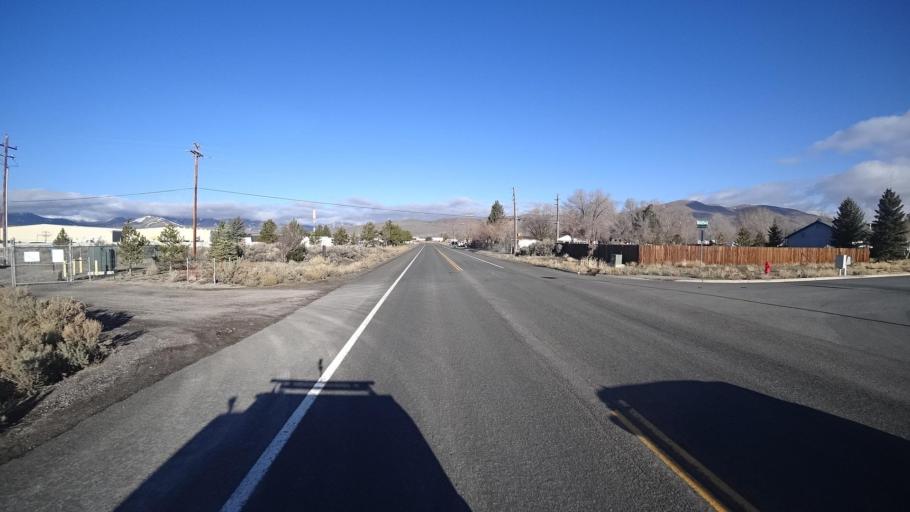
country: US
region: Nevada
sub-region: Washoe County
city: Cold Springs
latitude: 39.6730
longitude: -119.9688
